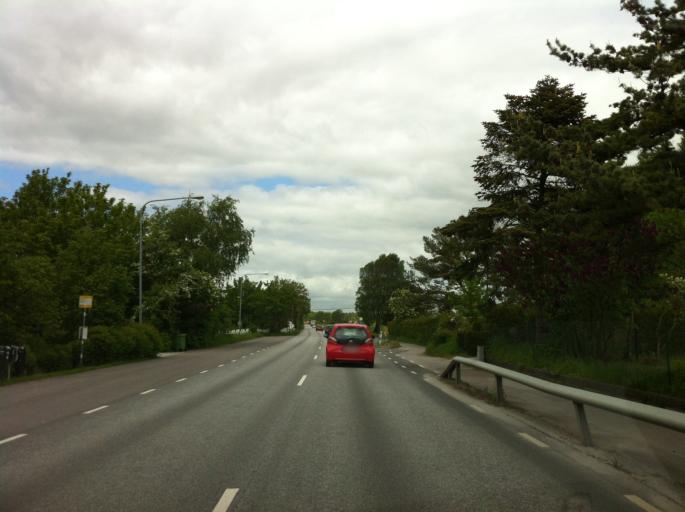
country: SE
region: Skane
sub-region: Kavlinge Kommun
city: Loddekopinge
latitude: 55.7812
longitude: 13.0069
